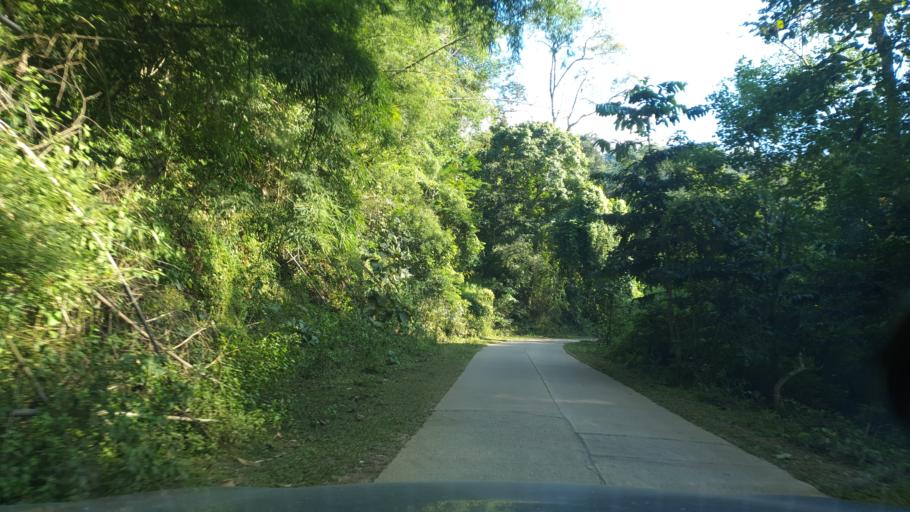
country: TH
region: Chiang Mai
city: Wiang Haeng
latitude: 19.3774
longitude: 98.7505
